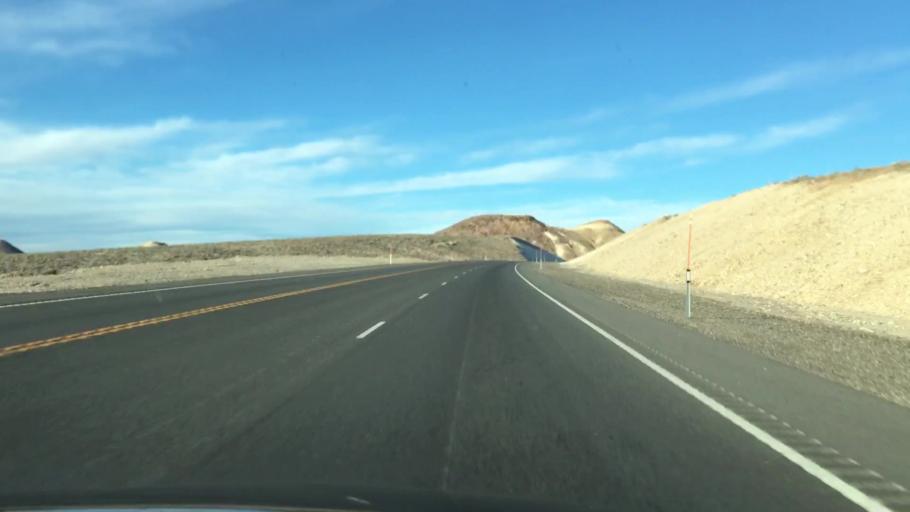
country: US
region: Nevada
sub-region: Nye County
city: Tonopah
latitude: 37.9901
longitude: -117.2733
